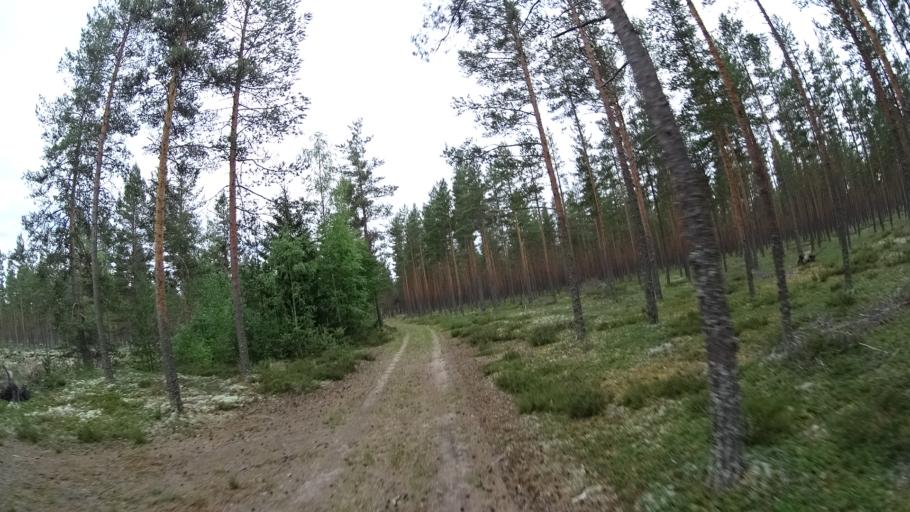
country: FI
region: Satakunta
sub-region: Pohjois-Satakunta
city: Jaemijaervi
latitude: 61.7695
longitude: 22.8015
